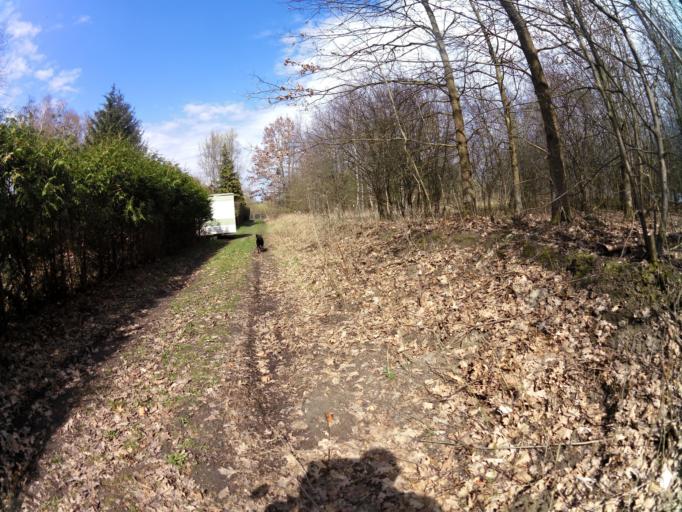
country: PL
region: West Pomeranian Voivodeship
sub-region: Powiat mysliborski
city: Mysliborz
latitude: 52.9403
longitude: 14.8612
